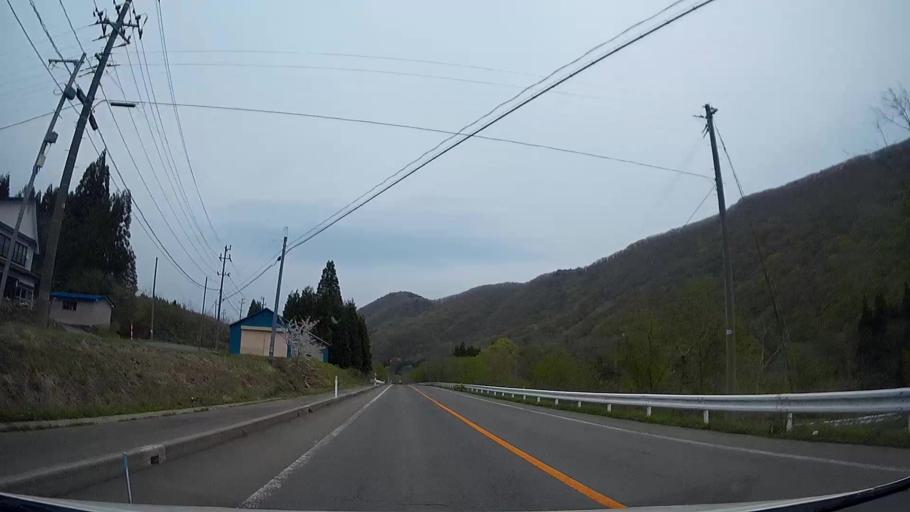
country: JP
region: Akita
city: Hanawa
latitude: 40.3471
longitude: 140.8403
